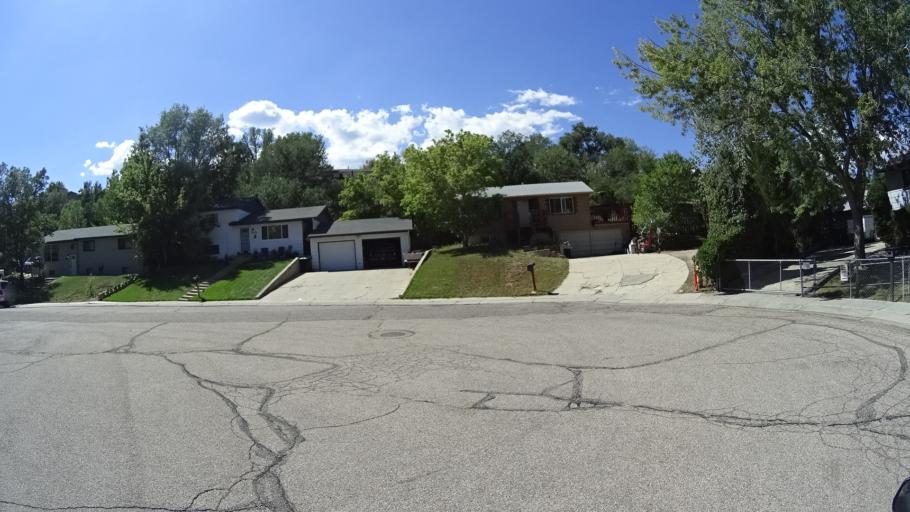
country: US
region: Colorado
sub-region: El Paso County
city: Colorado Springs
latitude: 38.8606
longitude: -104.8540
